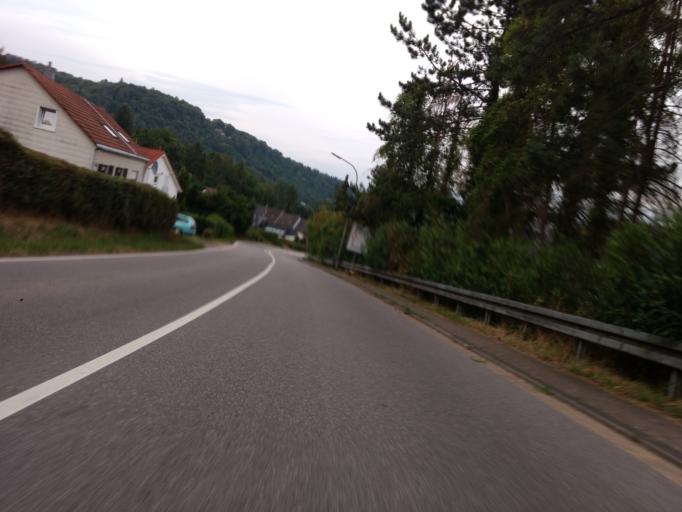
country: DE
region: Saarland
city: Wallerfangen
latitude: 49.3298
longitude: 6.6951
